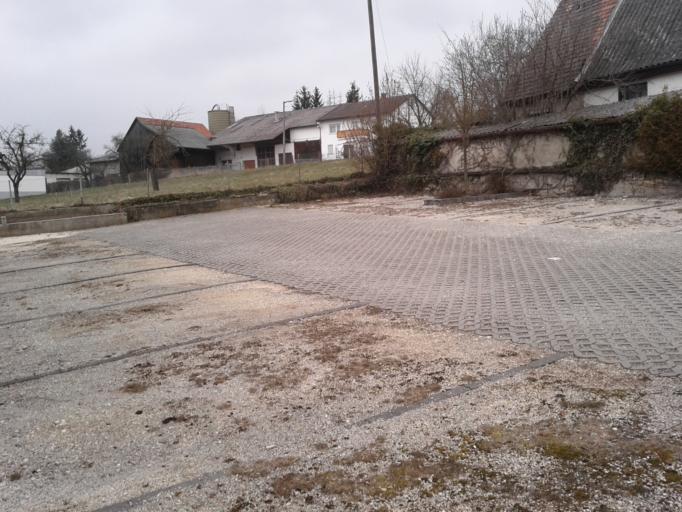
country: DE
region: Bavaria
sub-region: Swabia
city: Guenzburg
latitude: 48.4436
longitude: 10.2833
